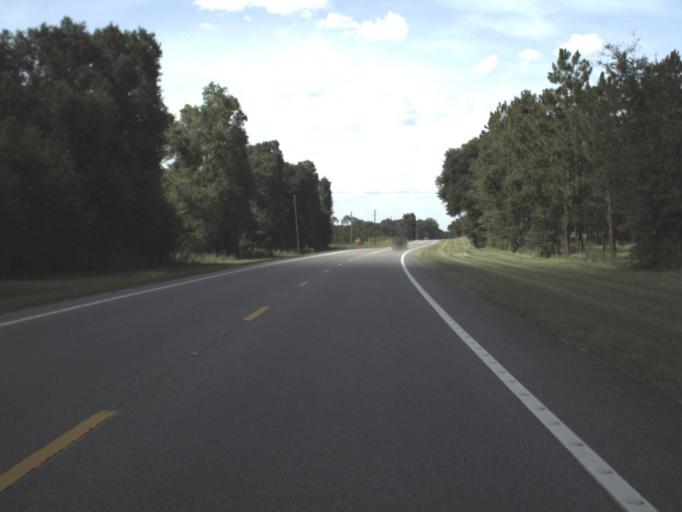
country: US
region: Florida
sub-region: Alachua County
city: High Springs
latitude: 29.8865
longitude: -82.7323
